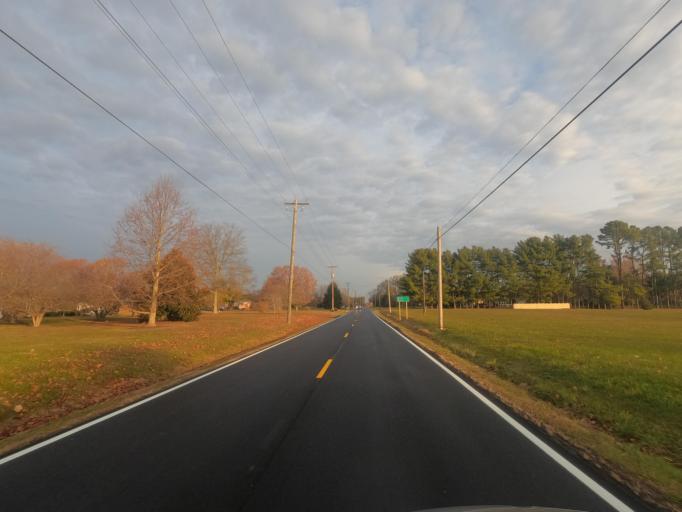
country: US
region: Delaware
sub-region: New Castle County
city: Townsend
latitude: 39.2644
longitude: -75.8378
